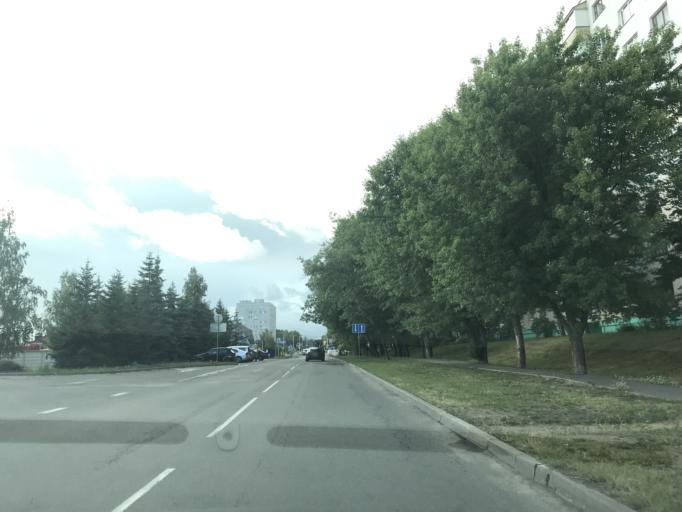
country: BY
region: Minsk
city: Minsk
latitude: 53.9496
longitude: 27.6016
